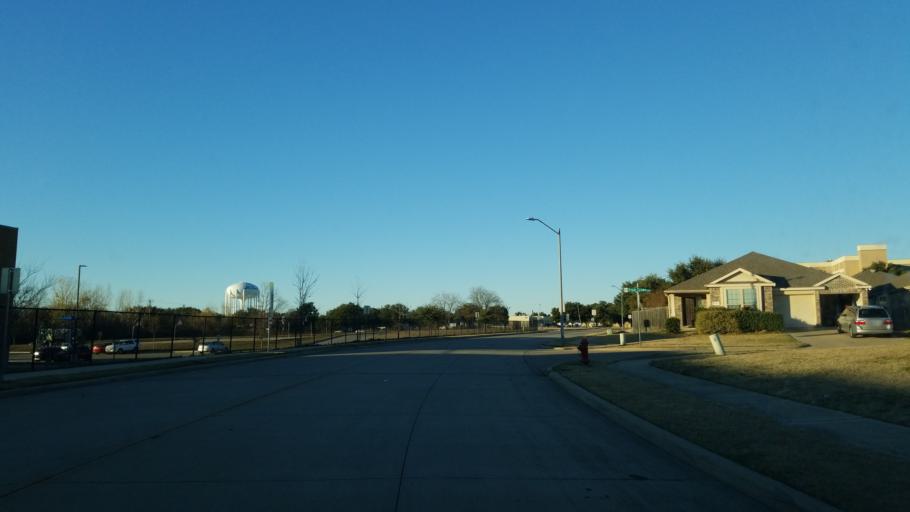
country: US
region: Texas
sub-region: Dallas County
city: Grand Prairie
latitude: 32.7300
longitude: -97.0494
